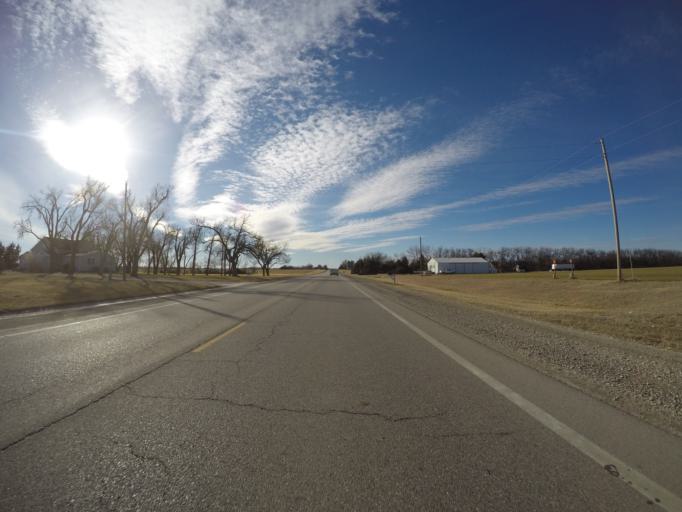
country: US
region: Kansas
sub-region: McPherson County
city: McPherson
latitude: 38.3768
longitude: -97.5481
